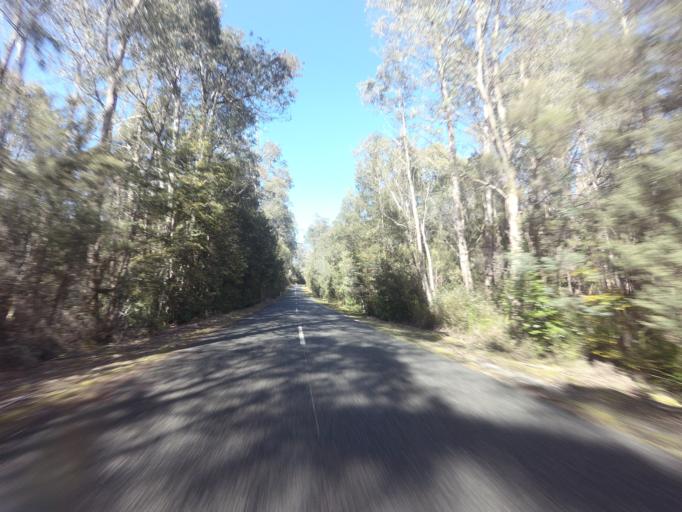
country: AU
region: Tasmania
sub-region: Derwent Valley
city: New Norfolk
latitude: -42.7356
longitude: 146.4241
